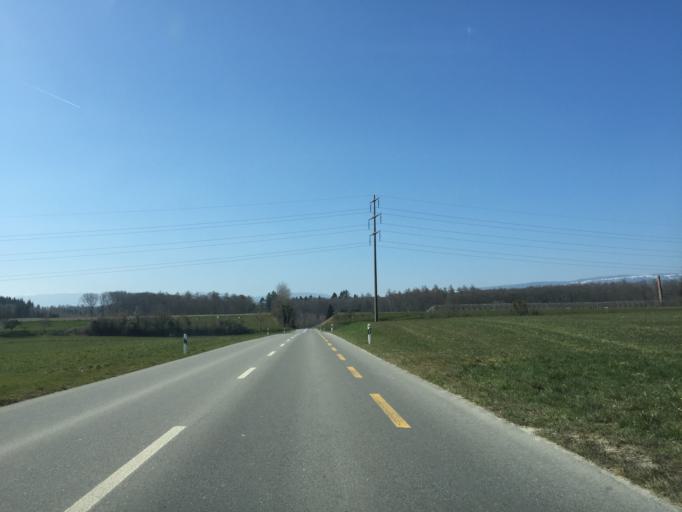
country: CH
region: Vaud
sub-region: Morges District
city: Cossonay
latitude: 46.6152
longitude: 6.4995
